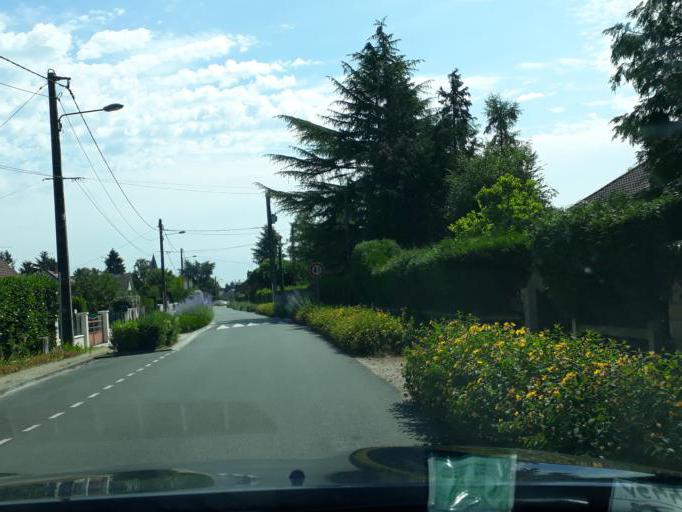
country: FR
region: Centre
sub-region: Departement du Loir-et-Cher
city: Vouzon
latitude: 47.6451
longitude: 2.0505
